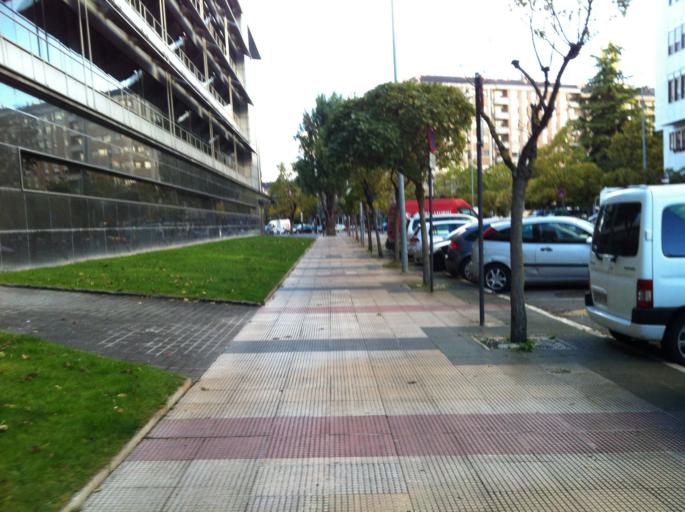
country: ES
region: Basque Country
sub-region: Provincia de Alava
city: Gasteiz / Vitoria
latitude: 42.8437
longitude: -2.6815
